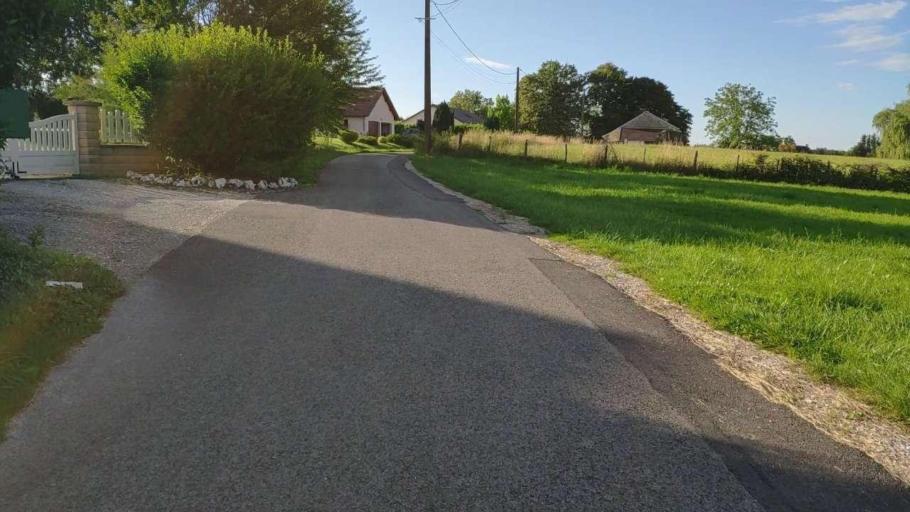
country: FR
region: Franche-Comte
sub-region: Departement du Jura
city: Bletterans
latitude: 46.7823
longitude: 5.4833
